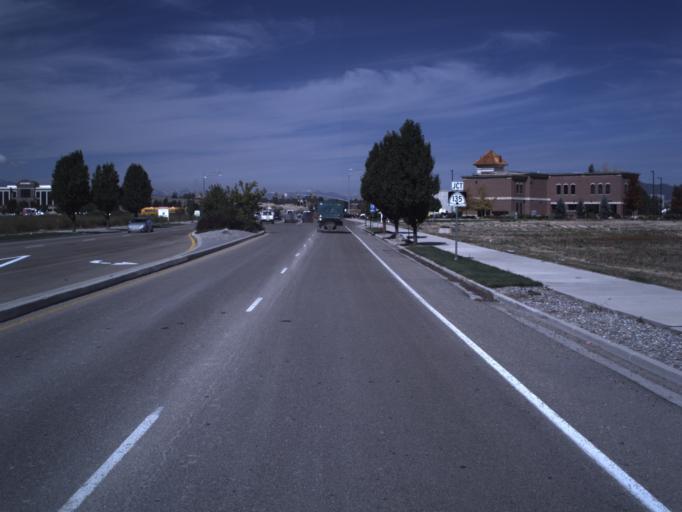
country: US
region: Utah
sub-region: Utah County
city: Pleasant Grove
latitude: 40.3527
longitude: -111.7619
